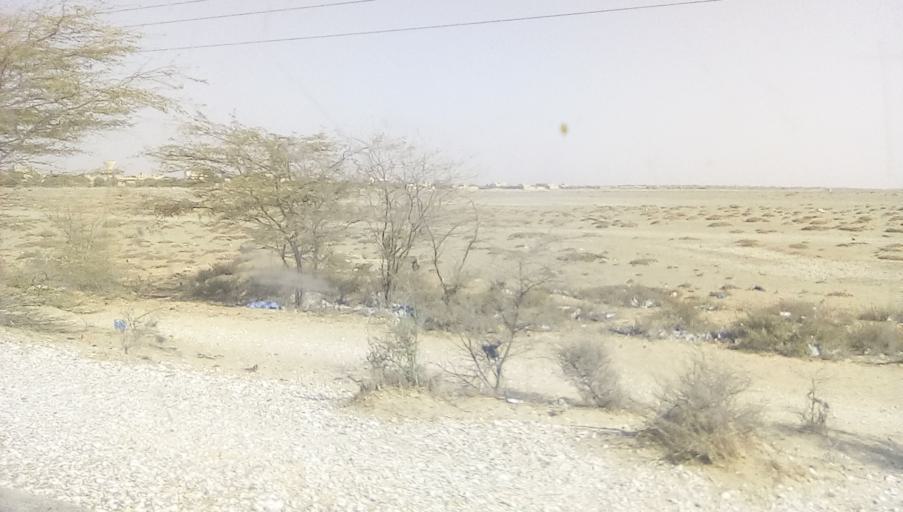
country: SN
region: Saint-Louis
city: Saint-Louis
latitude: 16.0391
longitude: -16.4523
